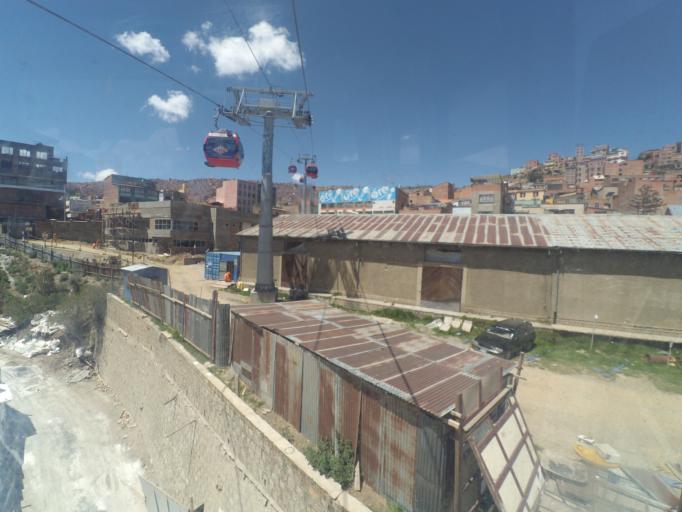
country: BO
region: La Paz
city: La Paz
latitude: -16.4918
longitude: -68.1451
